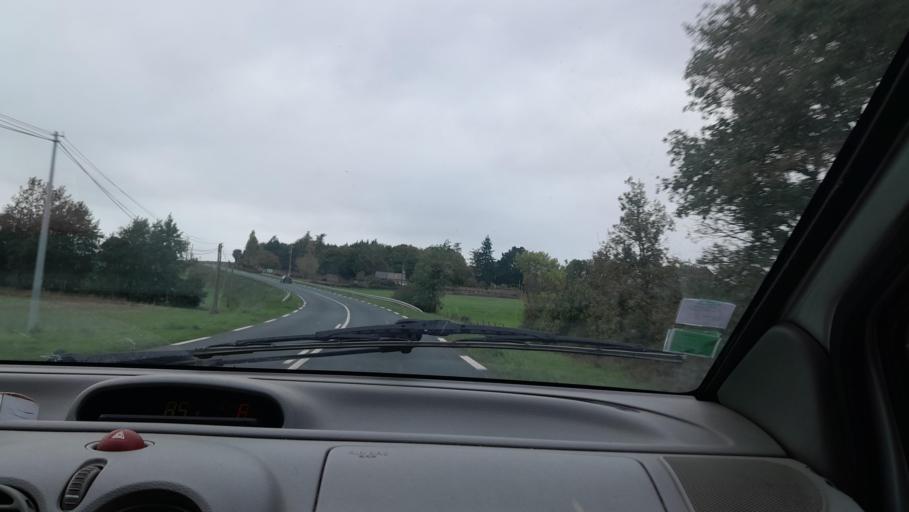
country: FR
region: Pays de la Loire
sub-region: Departement de la Loire-Atlantique
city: Saint-Mars-la-Jaille
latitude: 47.5012
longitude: -1.1768
